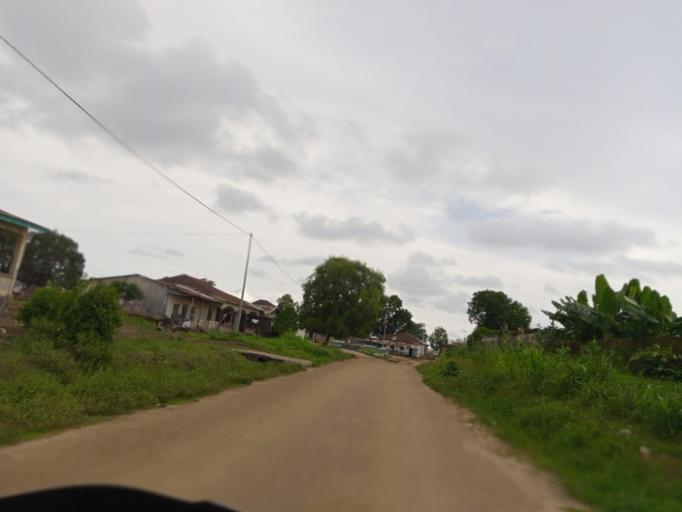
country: SL
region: Northern Province
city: Masoyila
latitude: 8.6015
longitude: -13.2013
